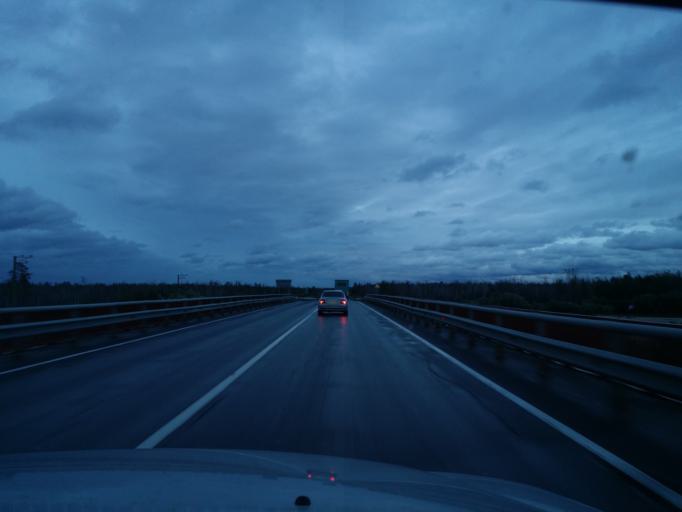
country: RU
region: Khanty-Mansiyskiy Avtonomnyy Okrug
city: Lokosovo
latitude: 61.4558
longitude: 74.6727
